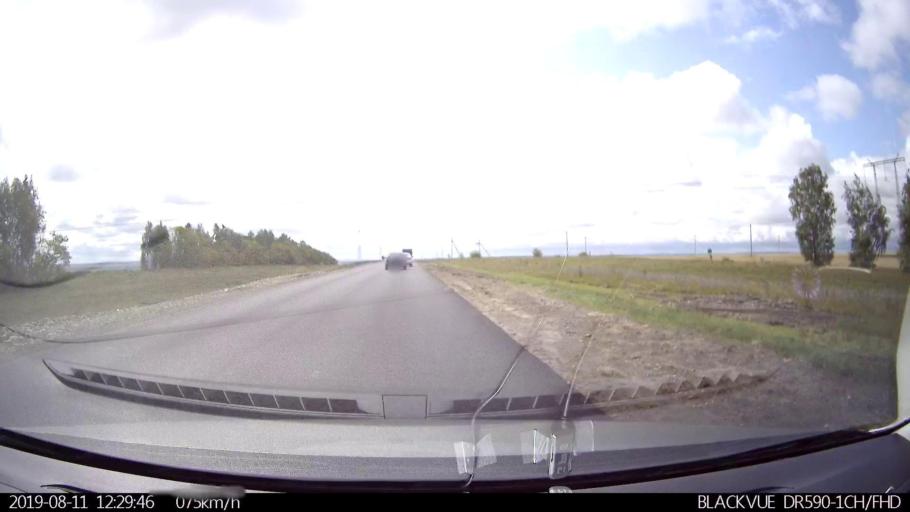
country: RU
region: Ulyanovsk
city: Ignatovka
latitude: 53.8317
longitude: 47.8996
